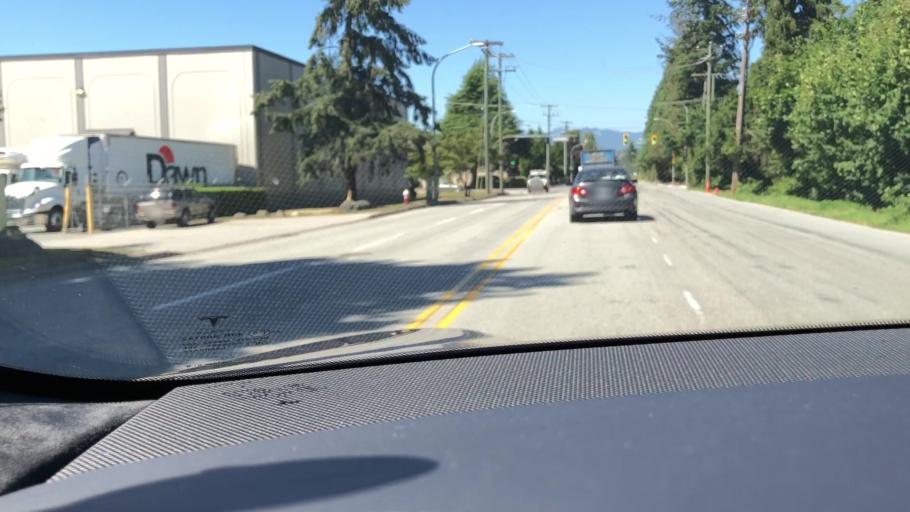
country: CA
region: British Columbia
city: Richmond
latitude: 49.1910
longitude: -123.0691
